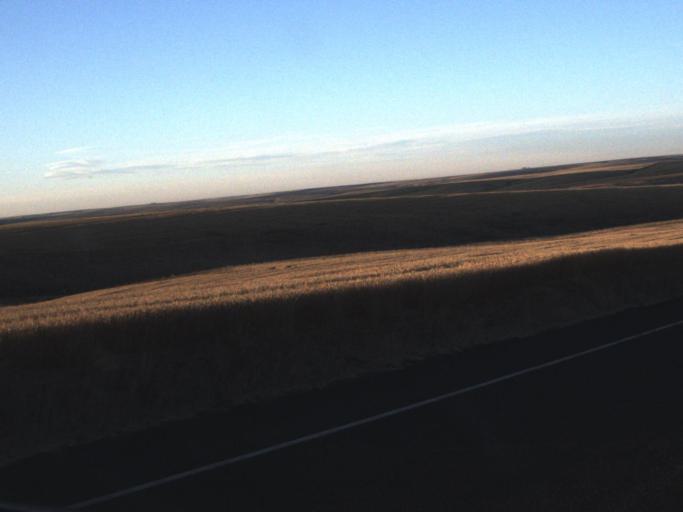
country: US
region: Washington
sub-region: Adams County
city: Ritzville
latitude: 46.9482
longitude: -118.5651
